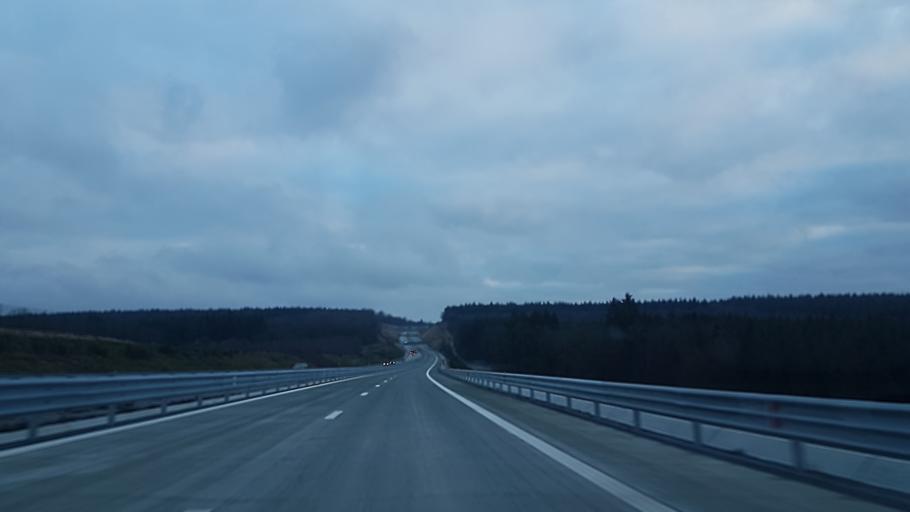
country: BE
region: Wallonia
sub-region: Province de Namur
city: Couvin
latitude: 50.0108
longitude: 4.5359
